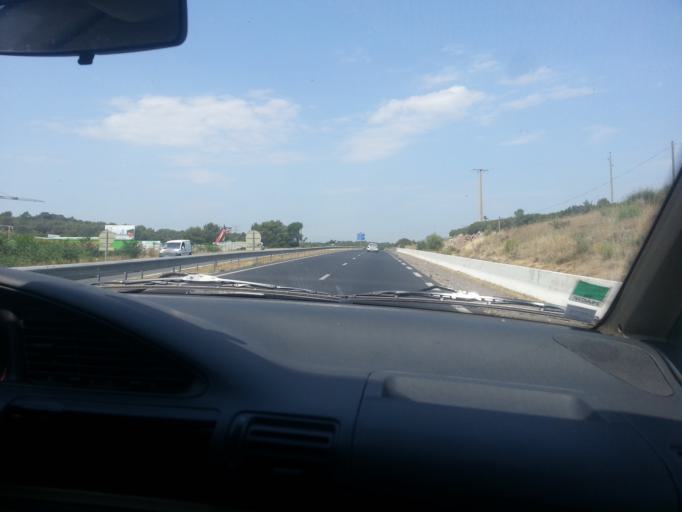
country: FR
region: Languedoc-Roussillon
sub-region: Departement de l'Herault
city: Grabels
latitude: 43.6303
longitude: 3.7683
